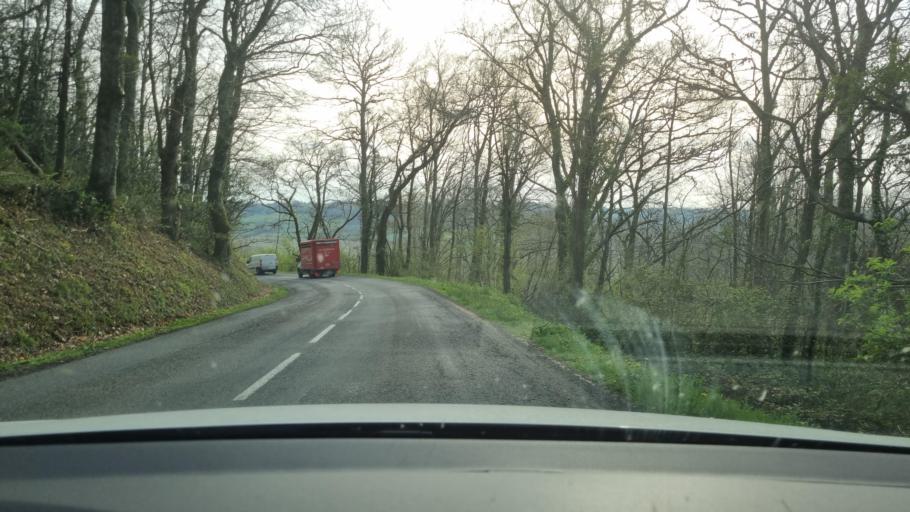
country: FR
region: Aquitaine
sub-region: Departement des Pyrenees-Atlantiques
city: Soumoulou
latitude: 43.3748
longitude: -0.1050
